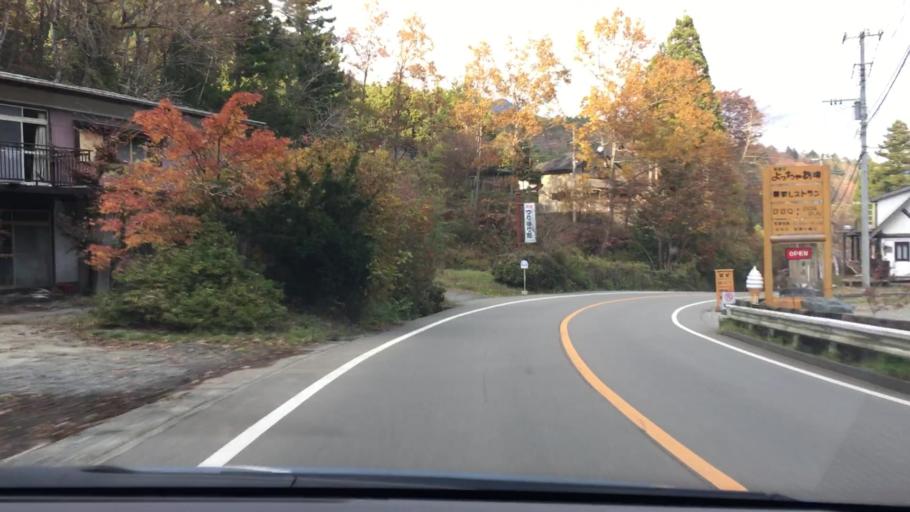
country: JP
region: Yamanashi
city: Otsuki
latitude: 35.4751
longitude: 138.9507
